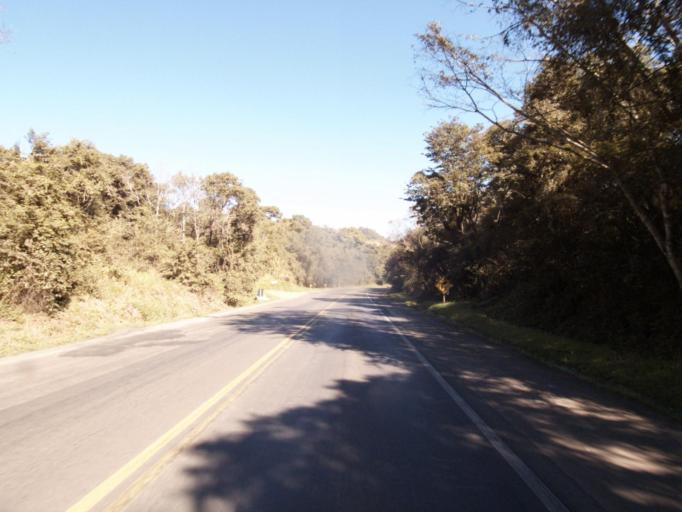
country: BR
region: Rio Grande do Sul
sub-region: Frederico Westphalen
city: Frederico Westphalen
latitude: -26.8167
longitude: -53.3626
